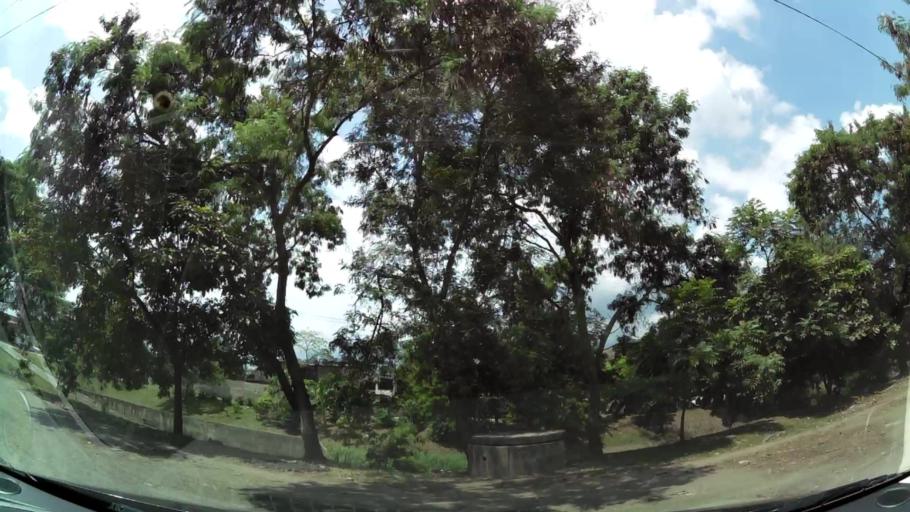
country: CO
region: Valle del Cauca
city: Cali
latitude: 3.4718
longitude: -76.4810
